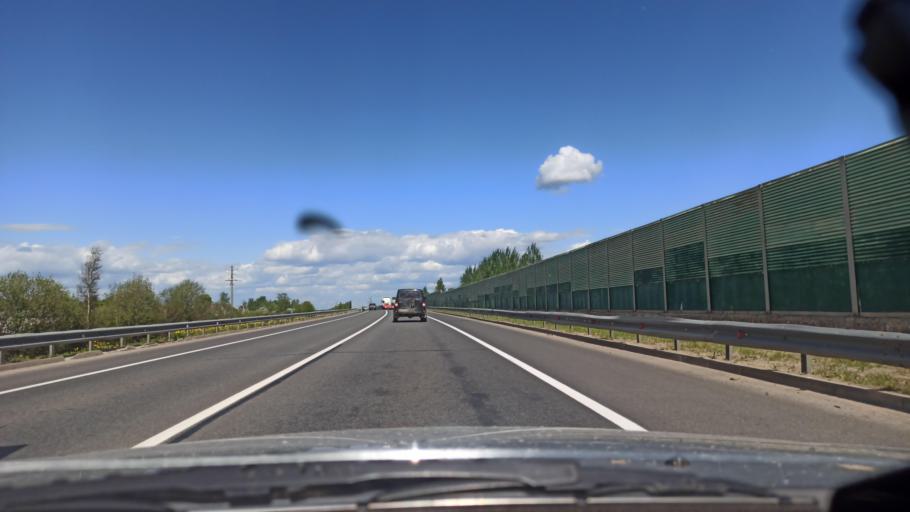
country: RU
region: Vologda
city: Vologda
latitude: 59.2812
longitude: 39.8378
